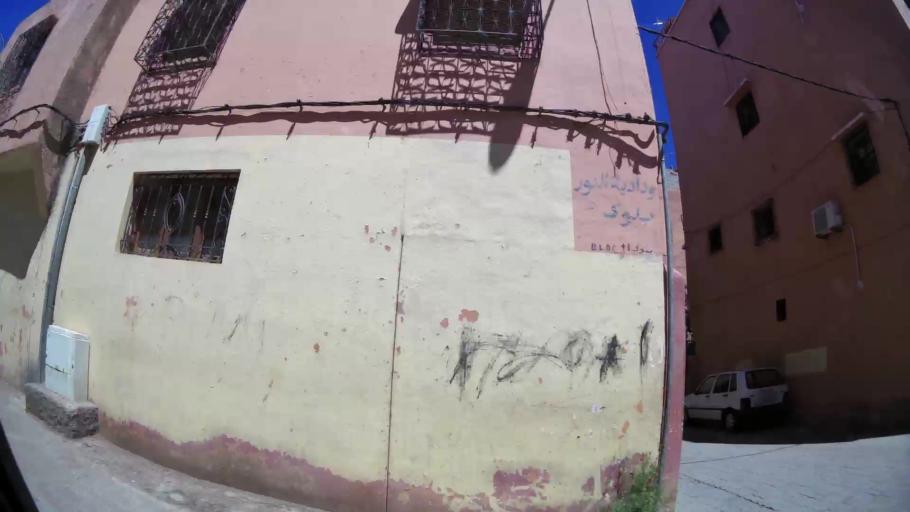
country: MA
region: Marrakech-Tensift-Al Haouz
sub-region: Marrakech
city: Marrakesh
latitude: 31.6516
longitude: -7.9917
